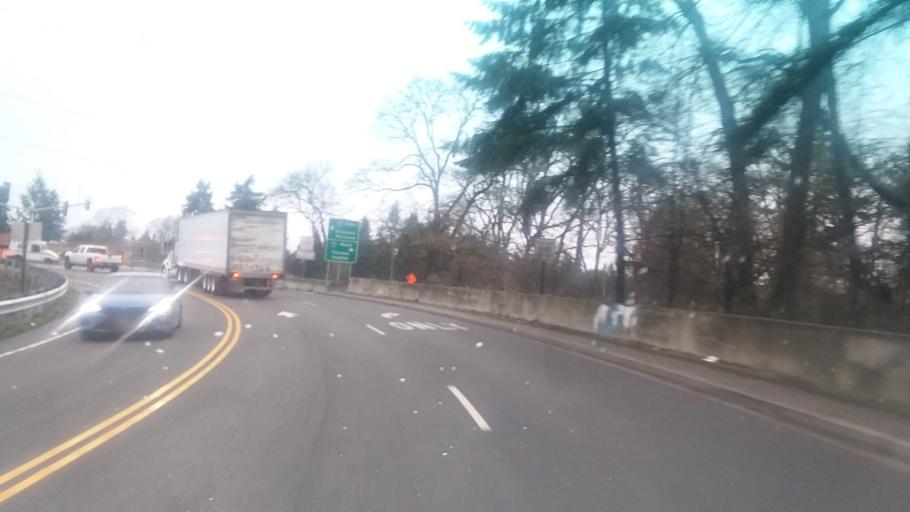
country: US
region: Washington
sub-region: Pierce County
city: Fort Lewis
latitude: 47.1261
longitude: -122.5417
